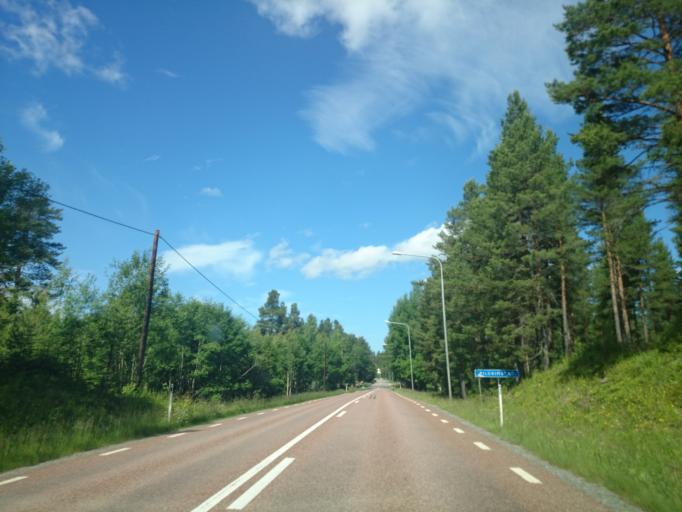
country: SE
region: Jaemtland
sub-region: OEstersunds Kommun
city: Brunflo
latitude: 62.9507
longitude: 15.0505
